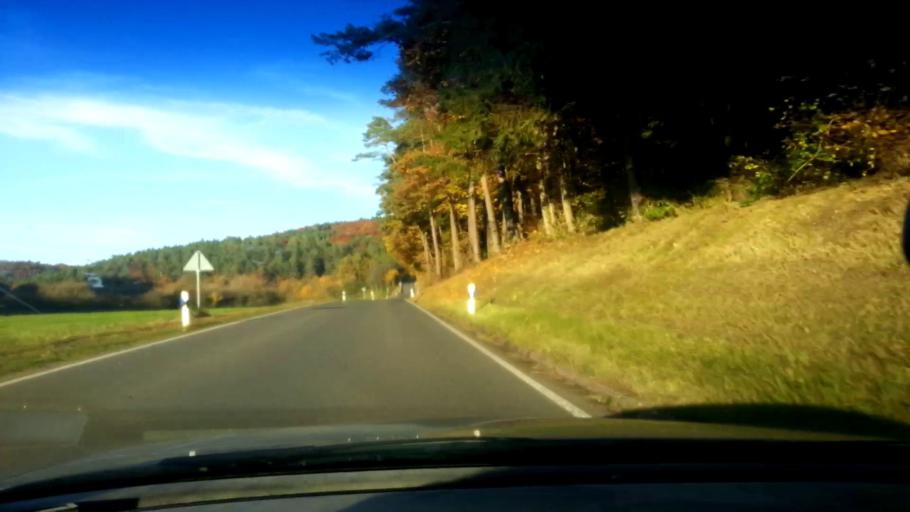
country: DE
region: Bavaria
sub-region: Upper Franconia
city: Unterleinleiter
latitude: 49.8463
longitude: 11.1953
